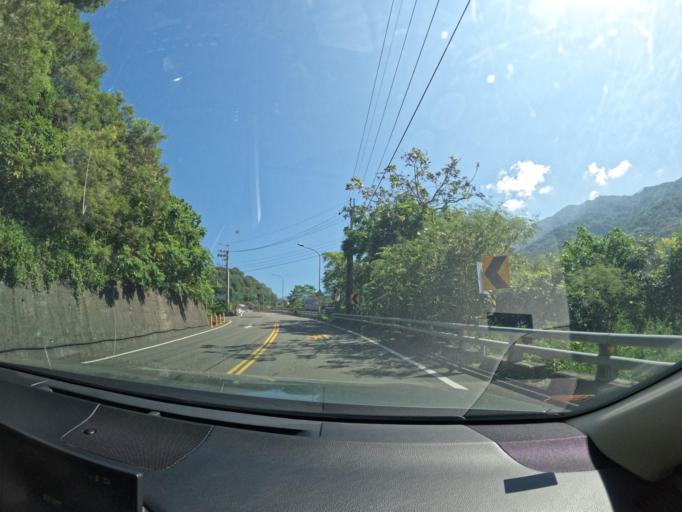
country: TW
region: Taiwan
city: Yujing
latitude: 23.1563
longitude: 120.7616
